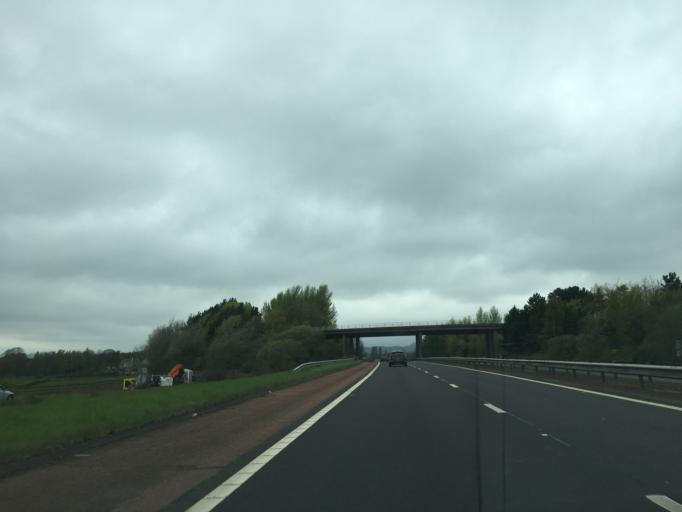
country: GB
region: Scotland
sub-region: Renfrewshire
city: Bishopton
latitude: 55.8990
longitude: -4.4839
